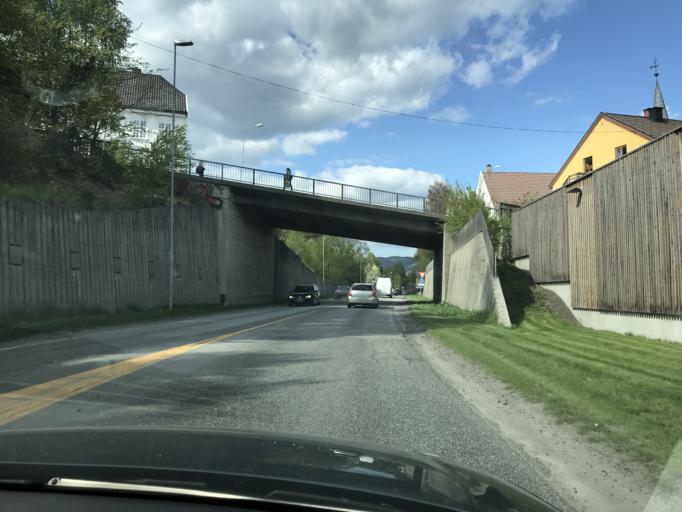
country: NO
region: Buskerud
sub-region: Kongsberg
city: Kongsberg
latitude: 59.6627
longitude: 9.6425
